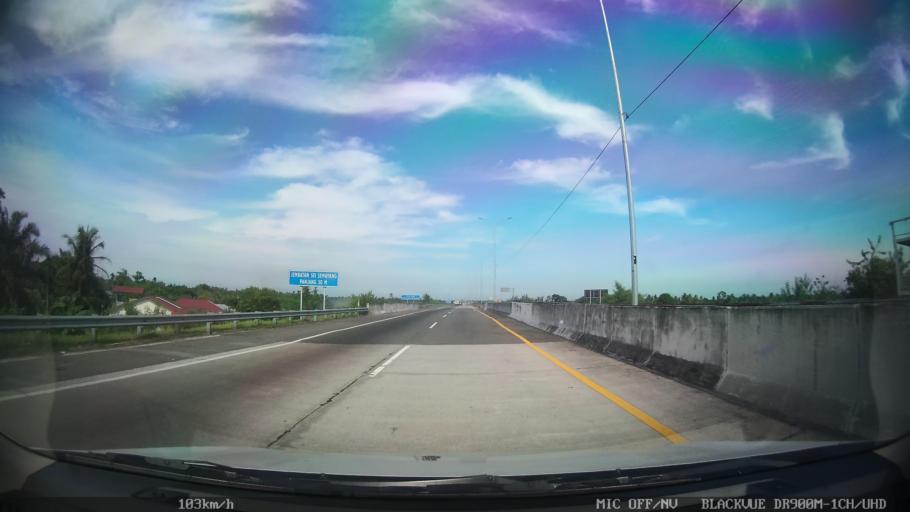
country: ID
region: North Sumatra
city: Sunggal
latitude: 3.6396
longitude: 98.5726
